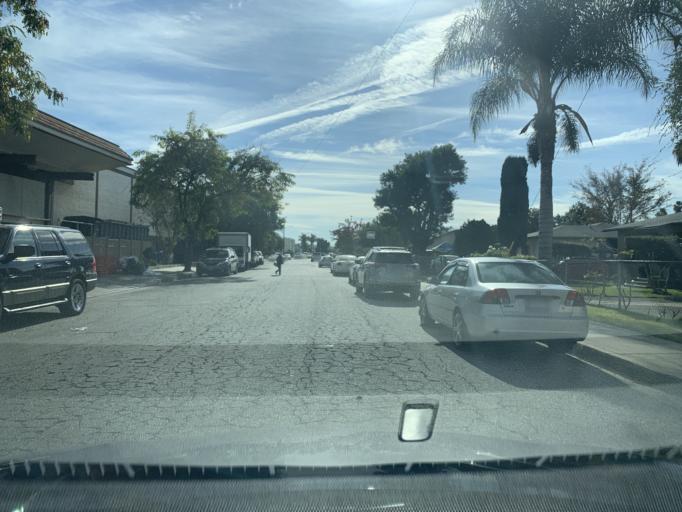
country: US
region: California
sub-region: Los Angeles County
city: South El Monte
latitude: 34.0622
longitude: -118.0529
